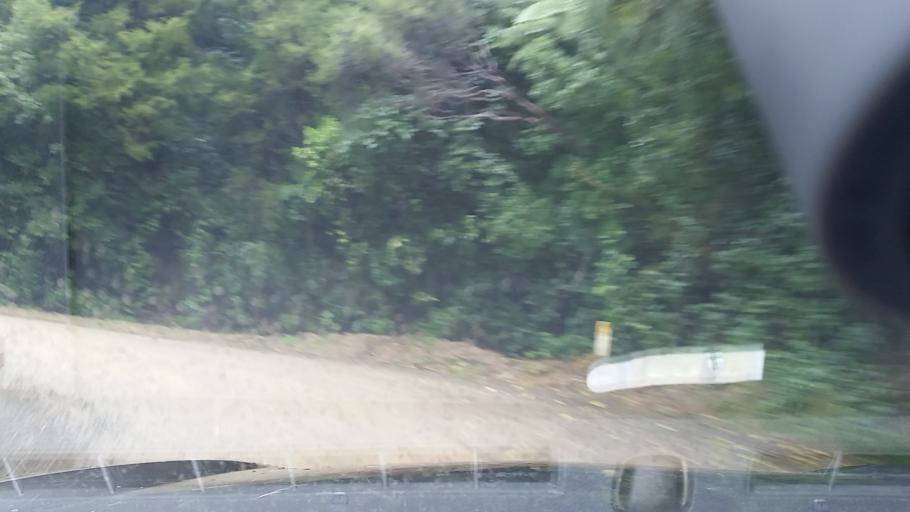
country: NZ
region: Marlborough
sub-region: Marlborough District
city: Picton
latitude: -41.3734
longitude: 174.0626
